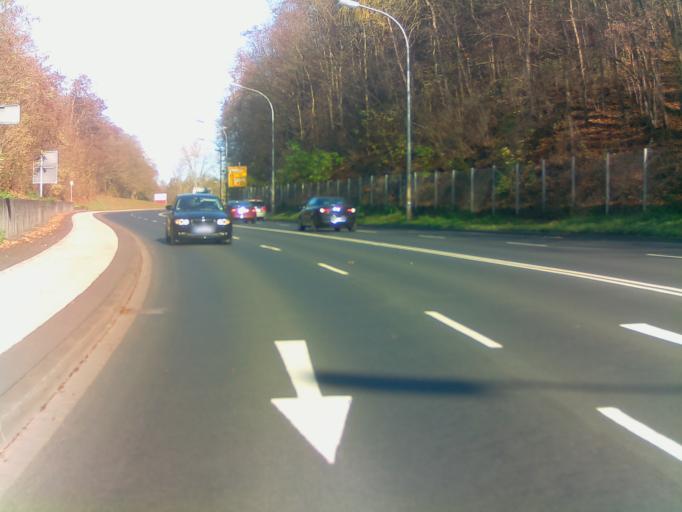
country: DE
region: Bavaria
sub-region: Regierungsbezirk Unterfranken
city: Bad Kissingen
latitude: 50.1890
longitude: 10.0803
